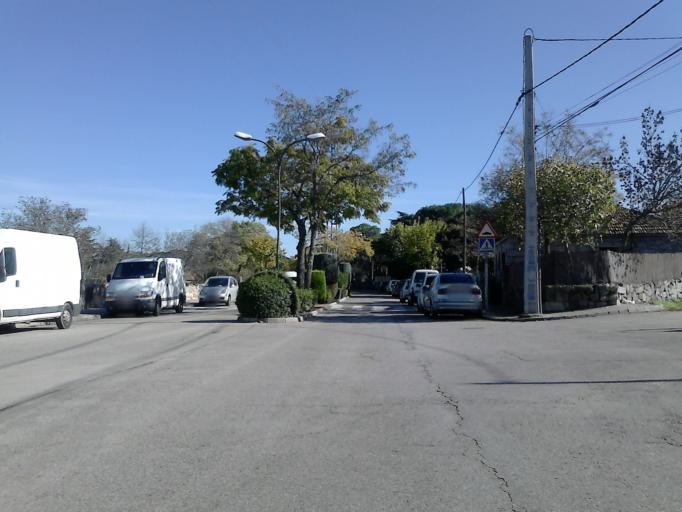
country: ES
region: Madrid
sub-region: Provincia de Madrid
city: Galapagar
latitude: 40.5747
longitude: -3.9985
